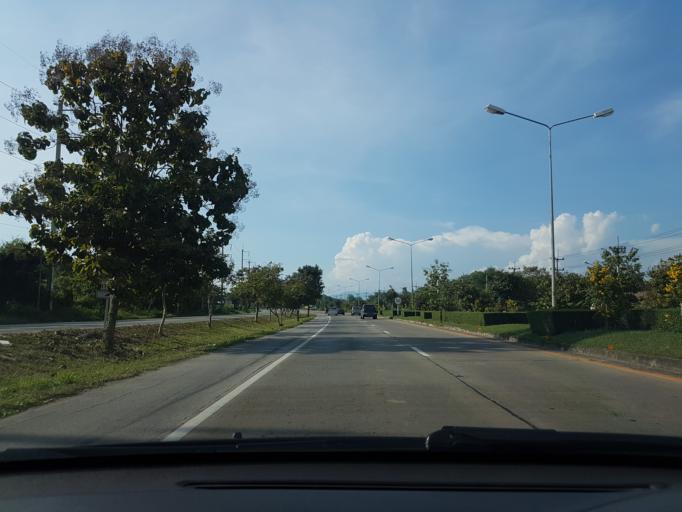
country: TH
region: Lampang
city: Lampang
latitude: 18.2844
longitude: 99.4488
